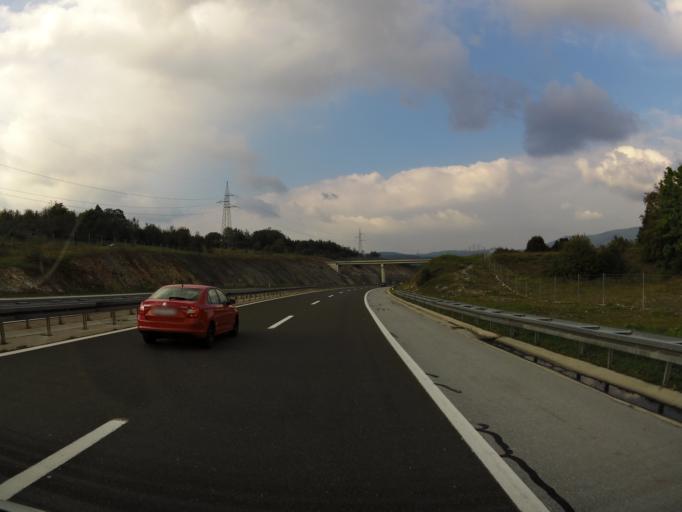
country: HR
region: Licko-Senjska
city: Brinje
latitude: 45.0447
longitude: 15.1781
